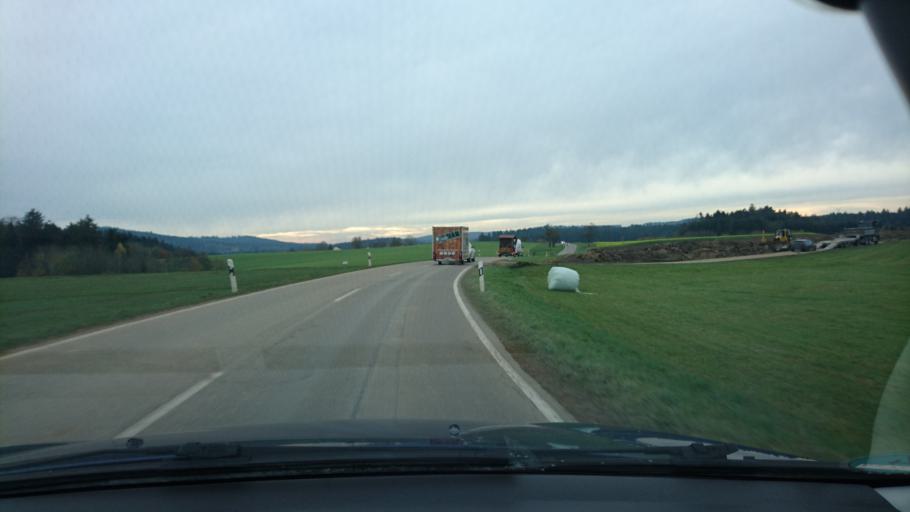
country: DE
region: Baden-Wuerttemberg
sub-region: Regierungsbezirk Stuttgart
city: Gschwend
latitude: 48.9202
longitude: 9.7072
